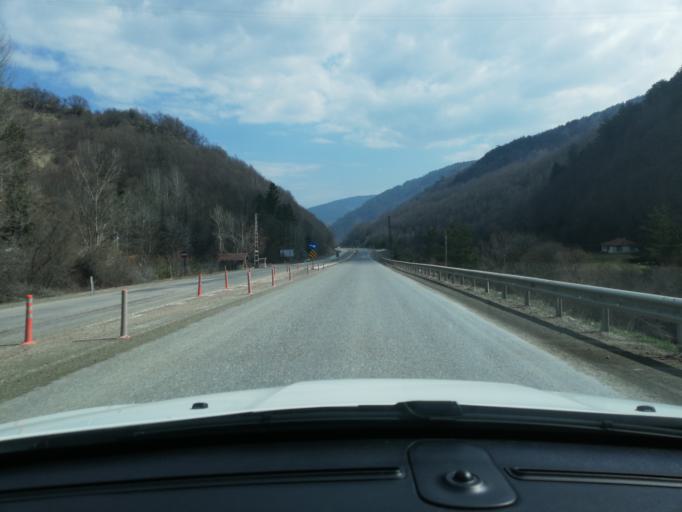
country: TR
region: Kastamonu
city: Kuzyaka
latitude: 41.1143
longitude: 33.7493
